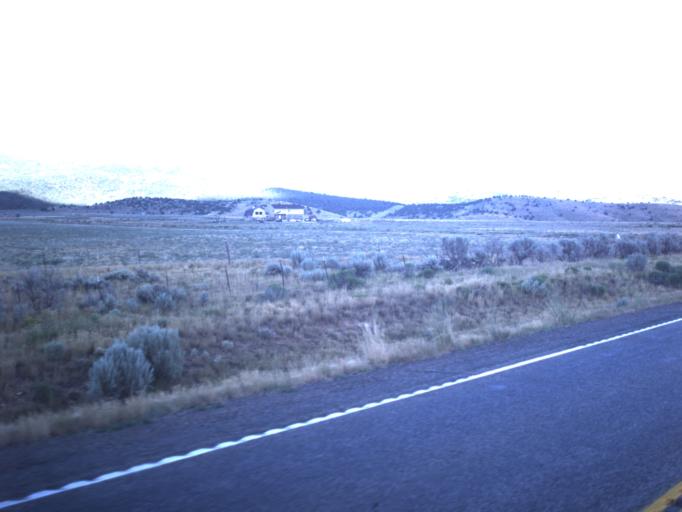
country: US
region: Utah
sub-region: Utah County
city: Woodland Hills
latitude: 39.8495
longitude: -111.5184
